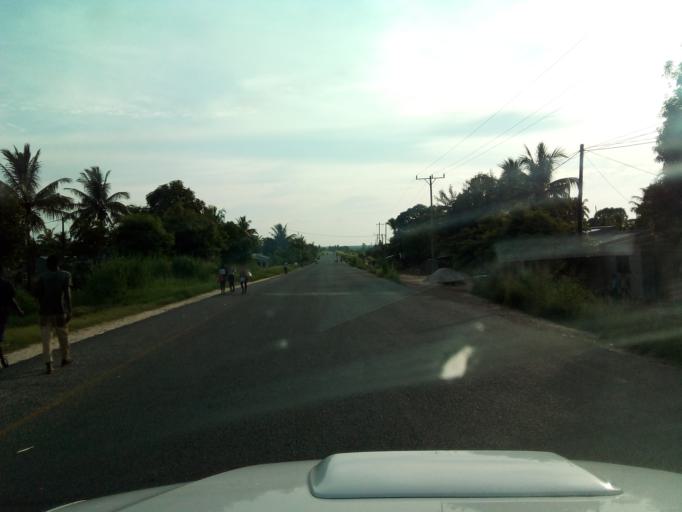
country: MZ
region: Zambezia
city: Quelimane
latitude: -17.4901
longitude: 37.0283
